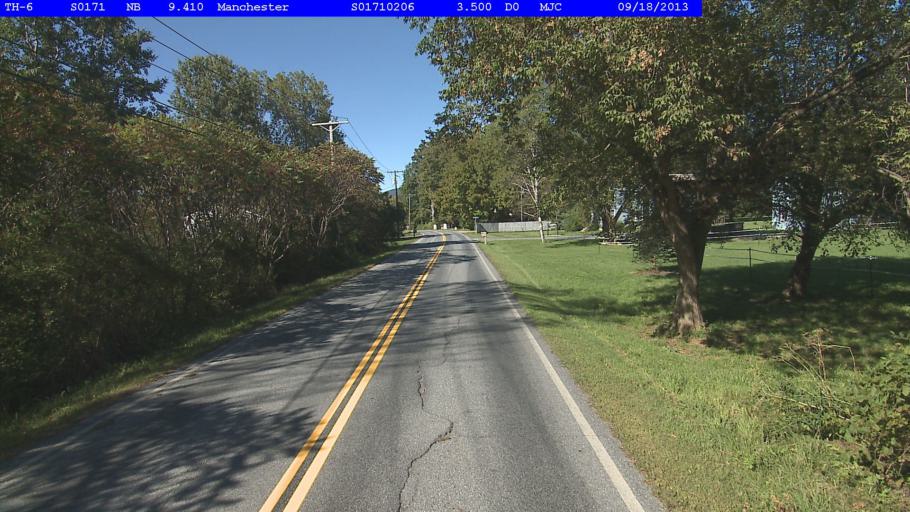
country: US
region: Vermont
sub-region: Bennington County
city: Manchester Center
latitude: 43.1549
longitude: -73.0515
